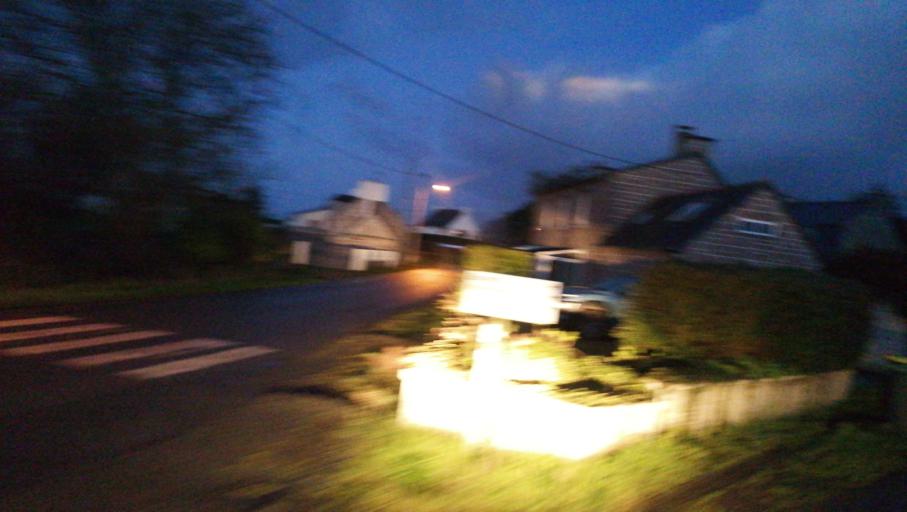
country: FR
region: Brittany
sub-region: Departement des Cotes-d'Armor
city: Plouha
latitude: 48.6710
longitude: -2.9625
